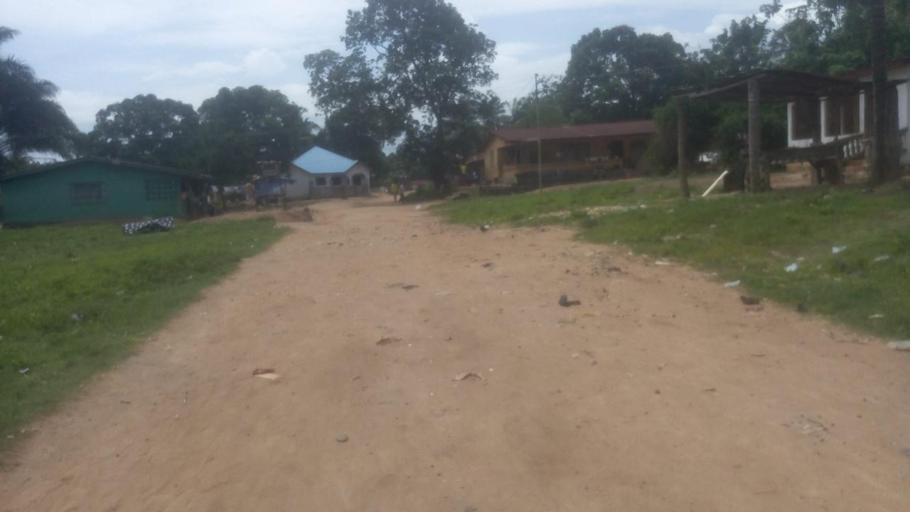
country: SL
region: Western Area
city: Freetown
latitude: 8.5202
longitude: -13.1497
